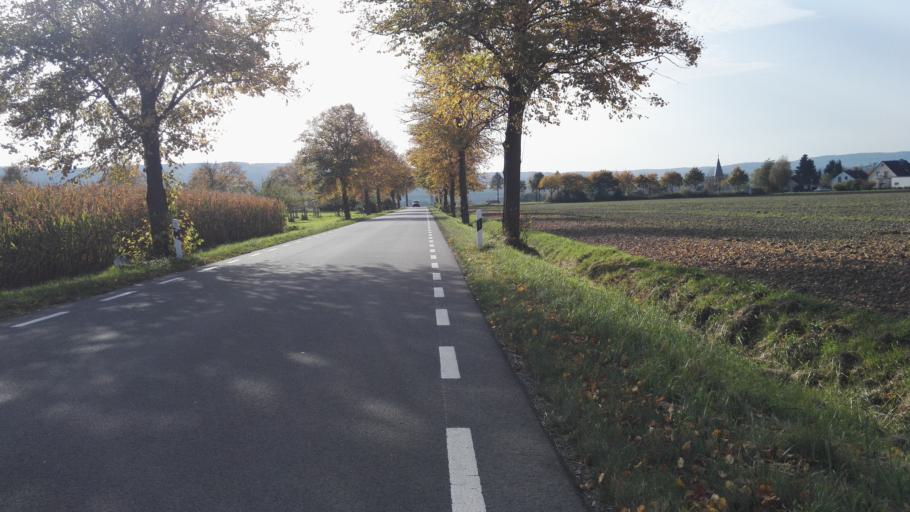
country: DE
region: Lower Saxony
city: Bad Salzdetfurth
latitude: 52.1125
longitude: 10.0039
